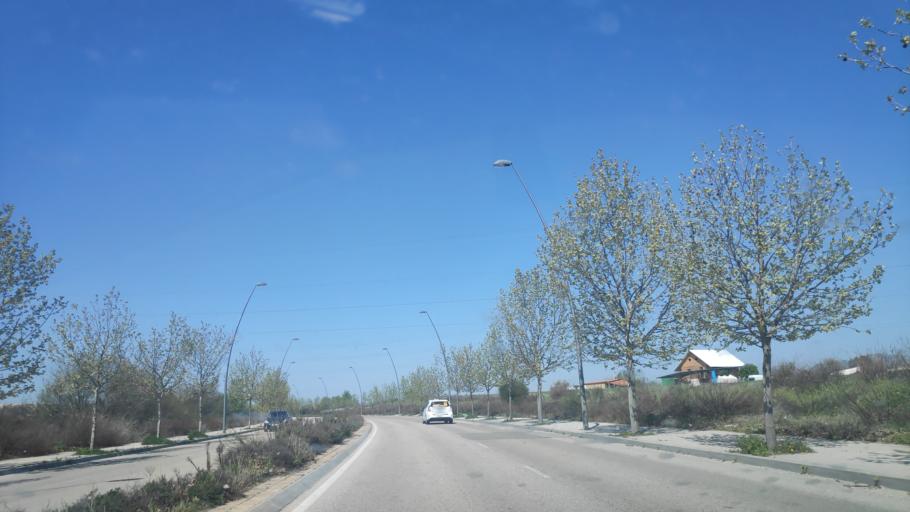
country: ES
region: Madrid
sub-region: Provincia de Madrid
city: Pinto
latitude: 40.2903
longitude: -3.6829
